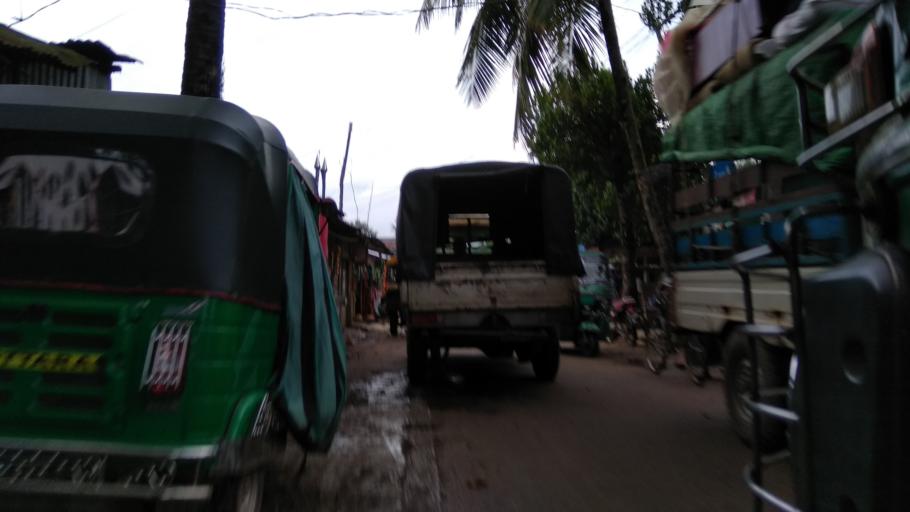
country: IN
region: Tripura
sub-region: Dhalai
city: Kamalpur
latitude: 24.2137
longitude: 91.8560
